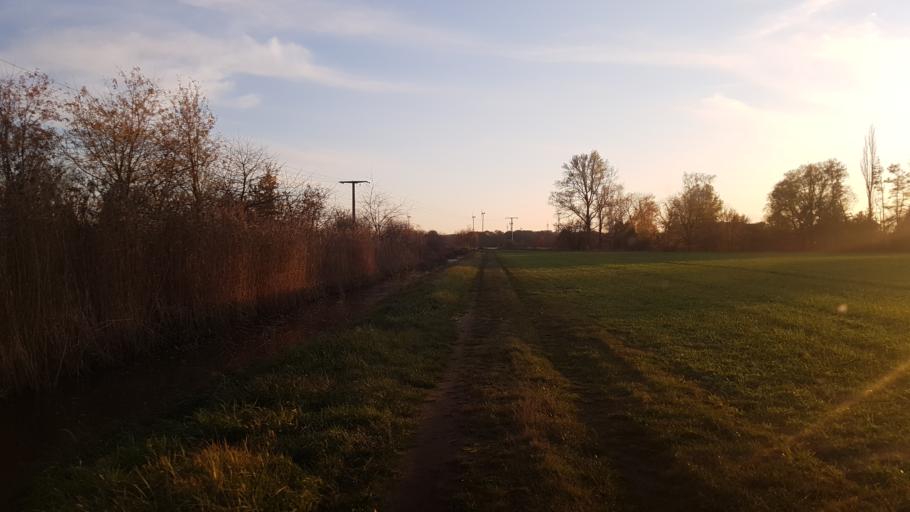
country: DE
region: Brandenburg
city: Schilda
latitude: 51.6013
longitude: 13.3154
